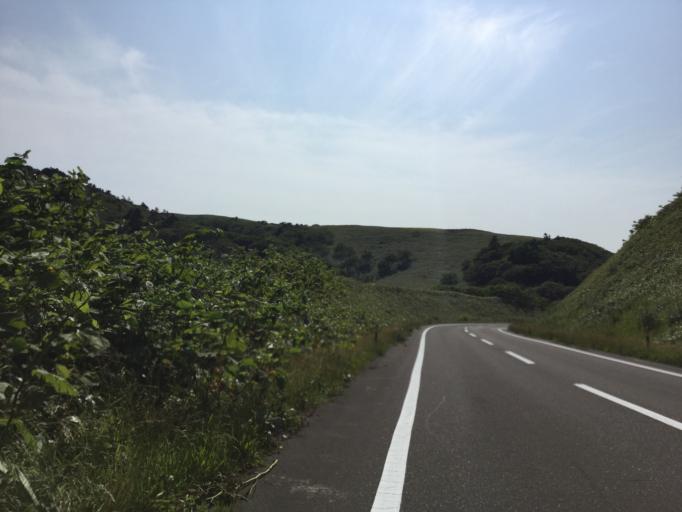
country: JP
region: Hokkaido
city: Makubetsu
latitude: 45.4963
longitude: 141.8993
